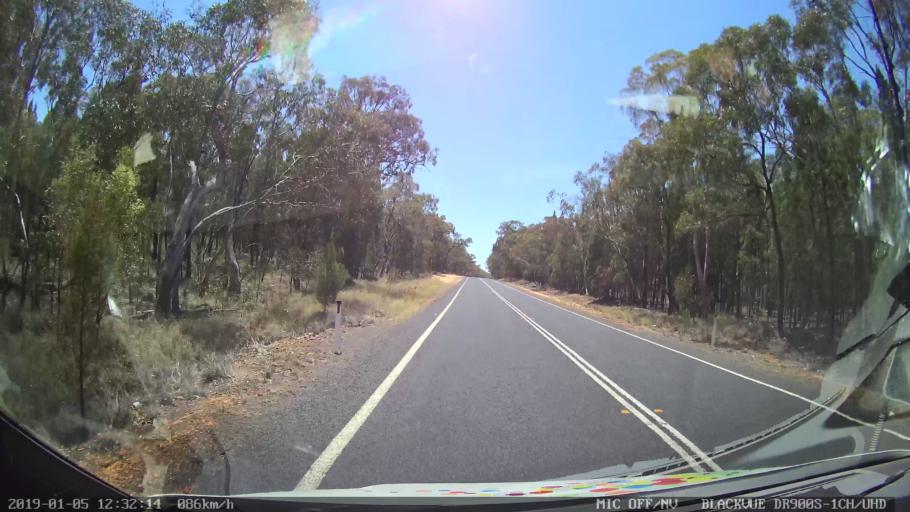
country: AU
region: New South Wales
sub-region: Warrumbungle Shire
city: Coonabarabran
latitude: -31.2179
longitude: 149.3766
